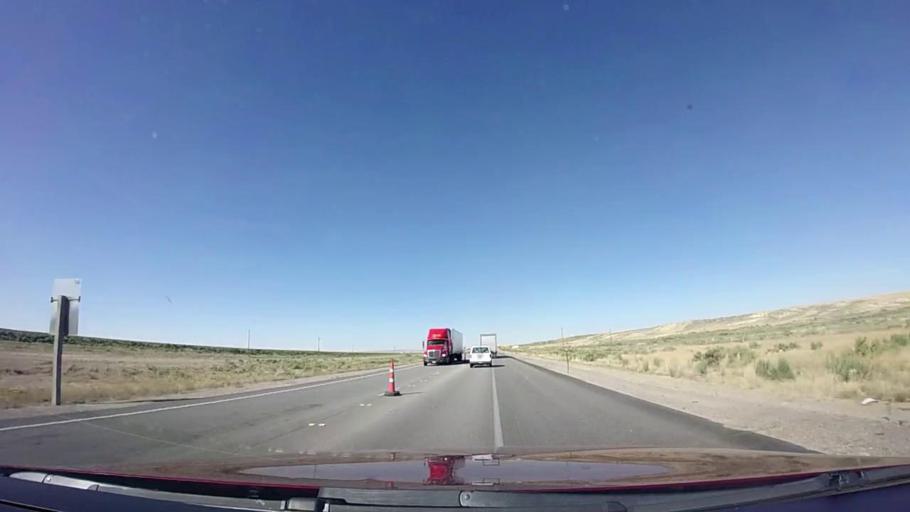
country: US
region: Wyoming
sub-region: Carbon County
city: Rawlins
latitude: 41.7023
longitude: -107.9052
